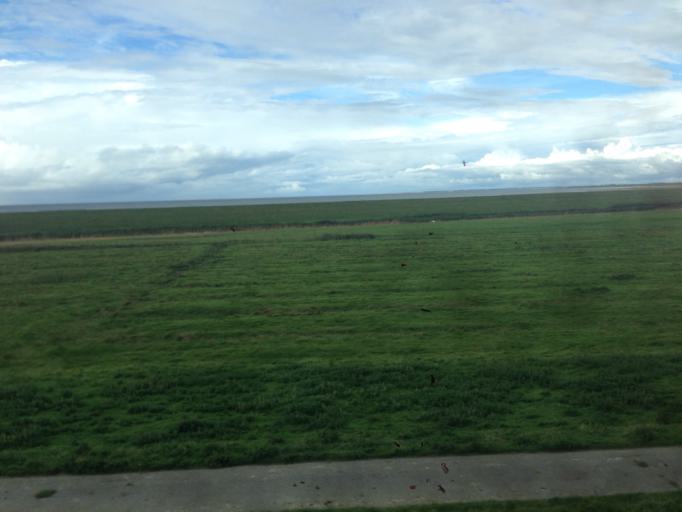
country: DE
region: Schleswig-Holstein
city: Friedrich-Wilhelm-Lubke-Koog
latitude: 54.8868
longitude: 8.6171
